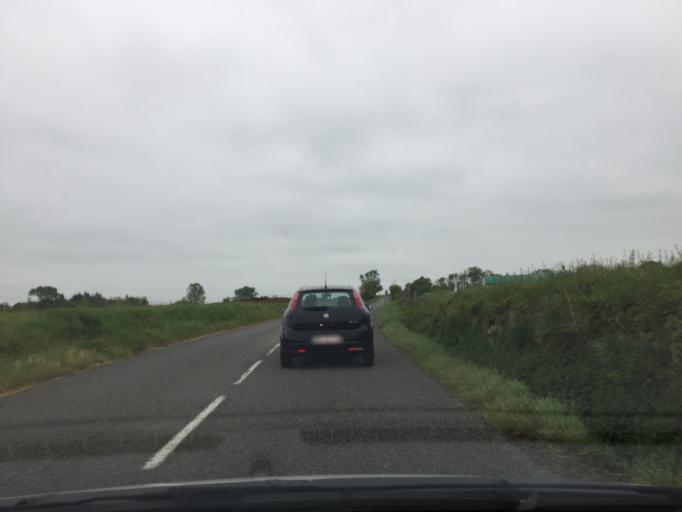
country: FR
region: Rhone-Alpes
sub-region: Departement du Rhone
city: Mornant
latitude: 45.5983
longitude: 4.6660
